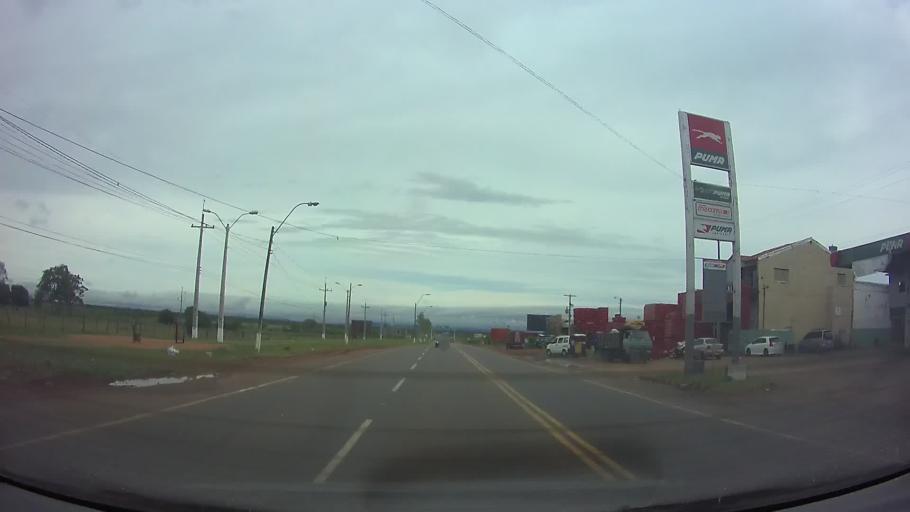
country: PY
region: Paraguari
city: Carapegua
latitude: -25.7620
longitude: -57.2331
